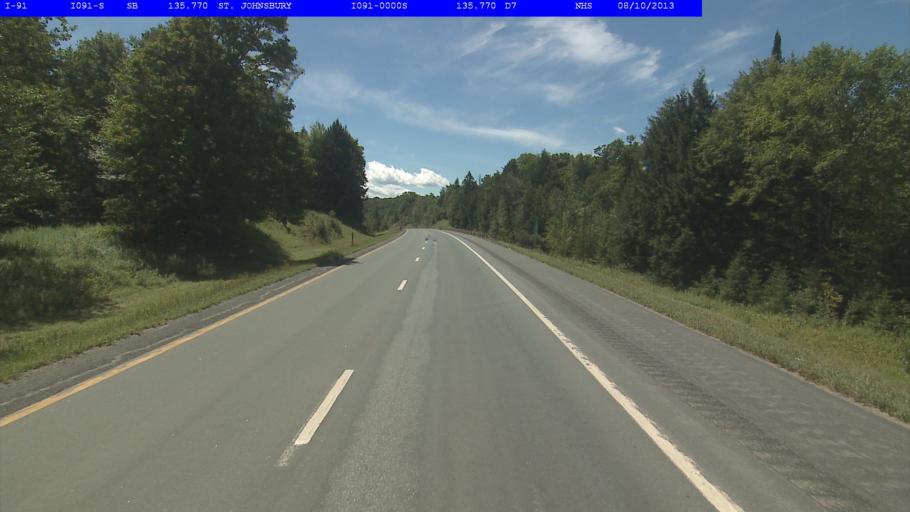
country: US
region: Vermont
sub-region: Caledonia County
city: Lyndon
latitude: 44.5004
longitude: -72.0209
